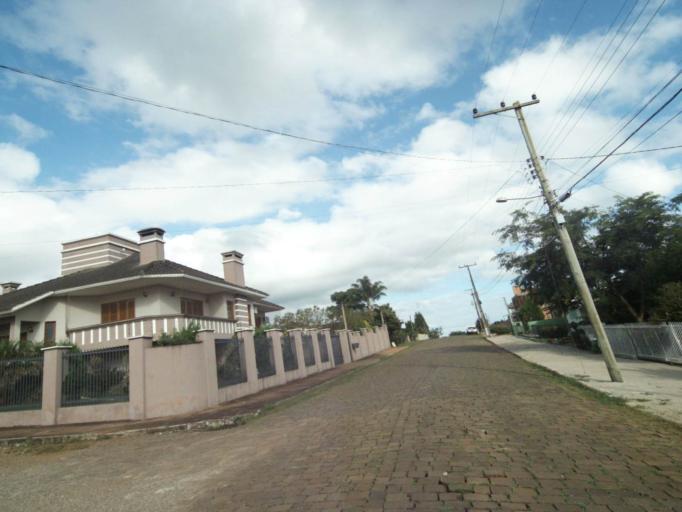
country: BR
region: Rio Grande do Sul
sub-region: Lagoa Vermelha
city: Lagoa Vermelha
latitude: -28.2060
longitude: -51.5163
